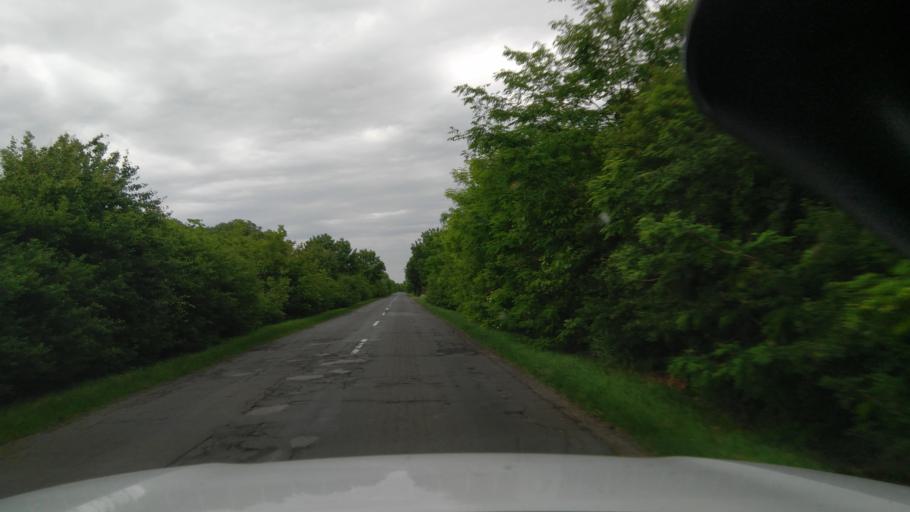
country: HU
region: Bekes
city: Bekescsaba
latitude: 46.6851
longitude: 21.1665
